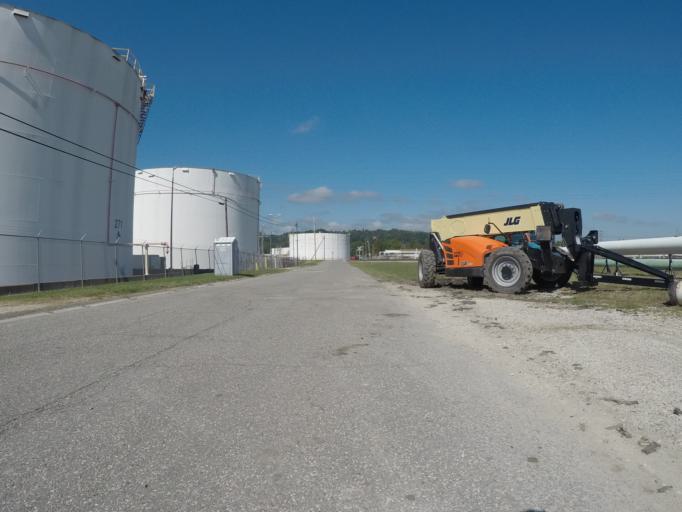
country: US
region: Ohio
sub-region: Lawrence County
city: South Point
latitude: 38.4062
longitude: -82.5874
